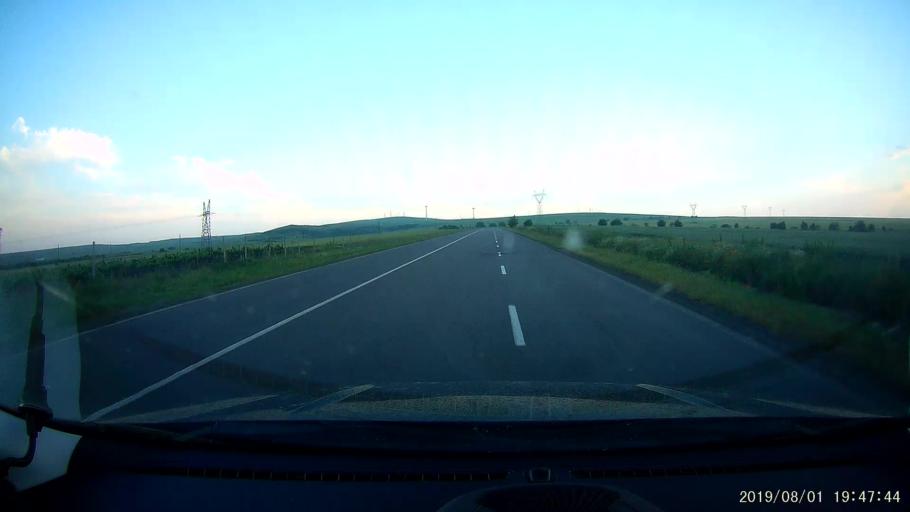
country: BG
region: Burgas
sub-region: Obshtina Karnobat
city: Karnobat
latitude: 42.6474
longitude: 26.9579
